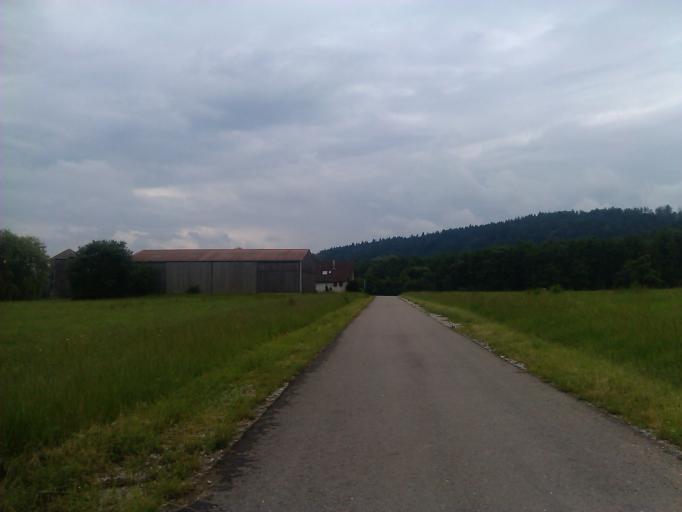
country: DE
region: Baden-Wuerttemberg
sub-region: Regierungsbezirk Stuttgart
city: Oberrot
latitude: 49.0053
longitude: 9.6726
